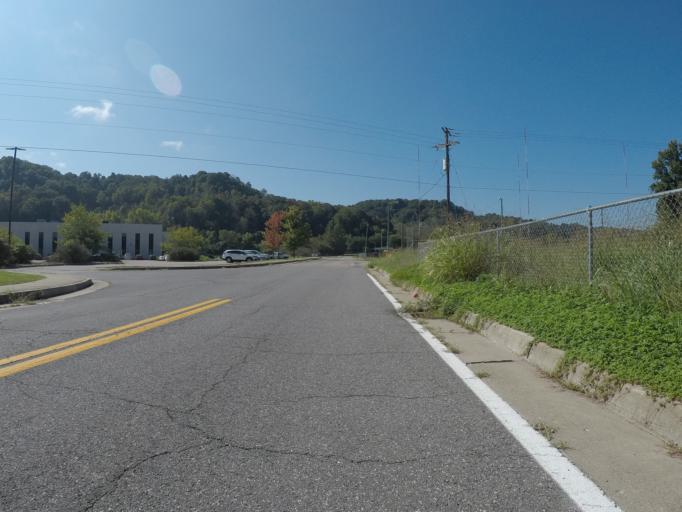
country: US
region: Ohio
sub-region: Lawrence County
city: Burlington
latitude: 38.4029
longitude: -82.4927
